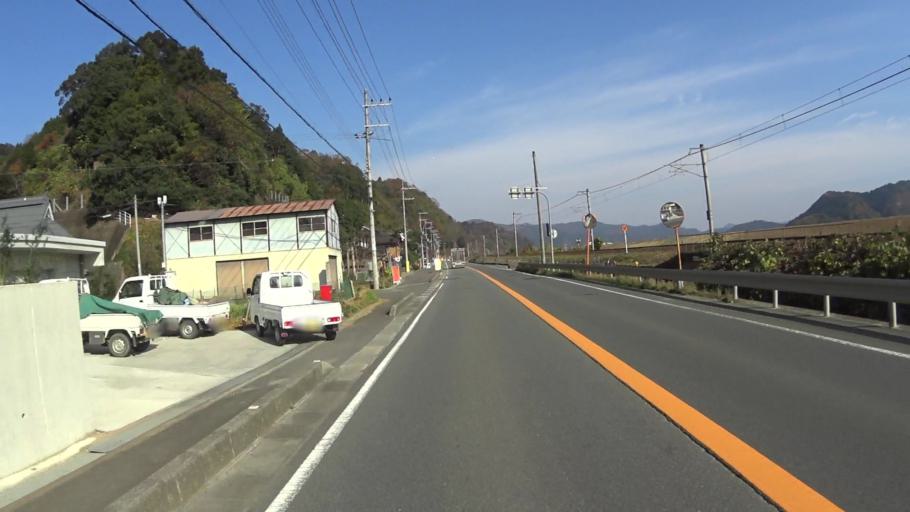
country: JP
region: Kyoto
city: Fukuchiyama
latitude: 35.3743
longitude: 135.1316
